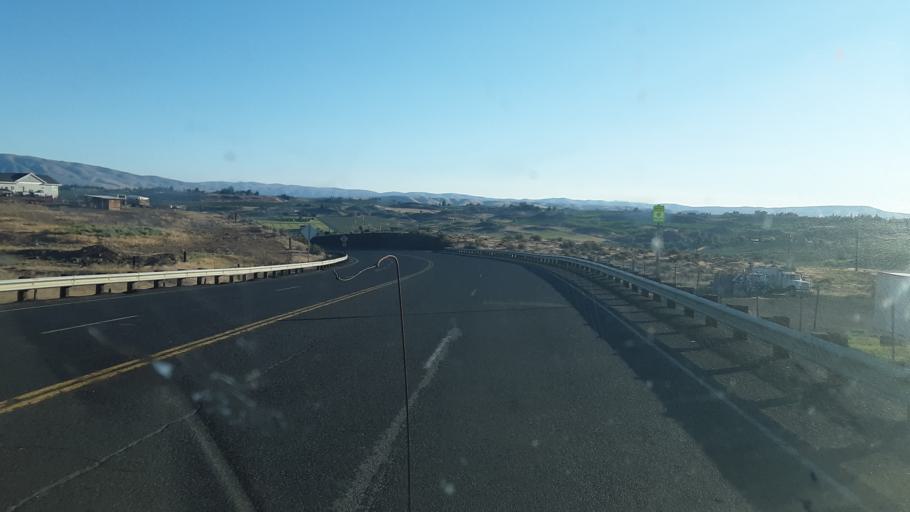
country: US
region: Washington
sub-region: Yakima County
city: Gleed
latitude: 46.6275
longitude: -120.6702
